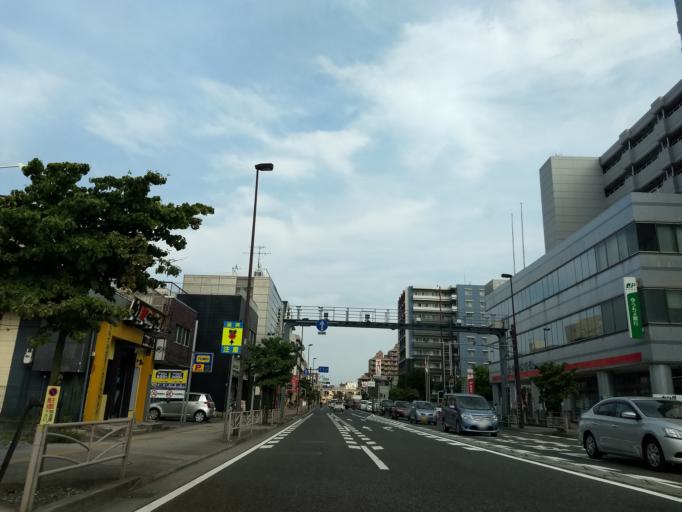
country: JP
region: Kanagawa
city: Yokohama
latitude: 35.4614
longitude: 139.5962
